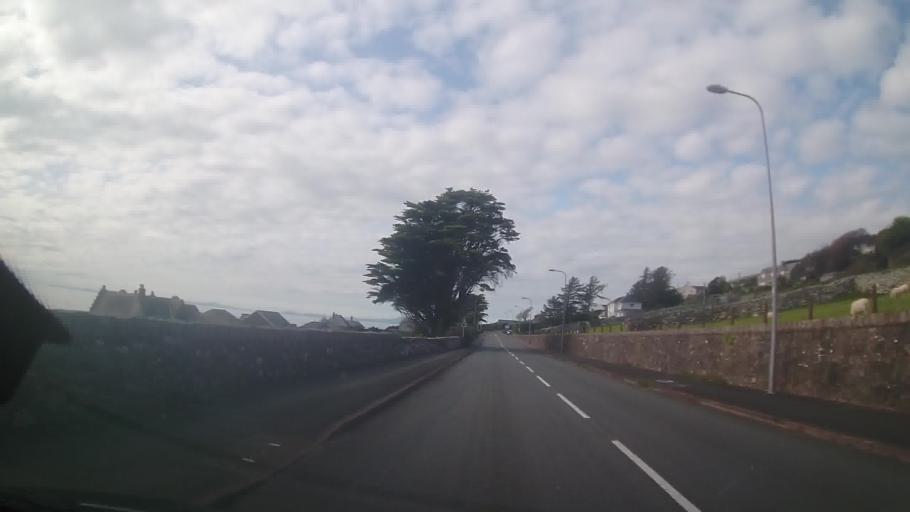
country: GB
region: Wales
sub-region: Gwynedd
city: Barmouth
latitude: 52.7376
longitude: -4.0714
